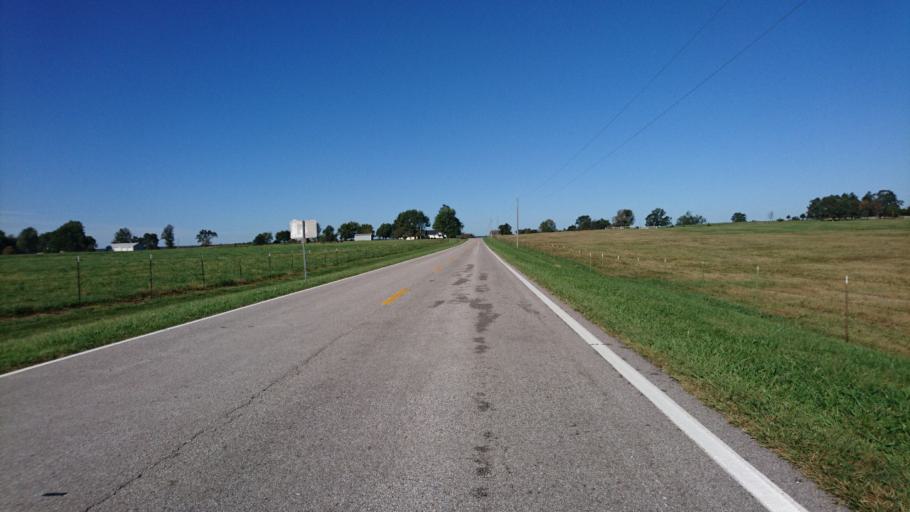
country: US
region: Missouri
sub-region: Greene County
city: Ash Grove
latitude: 37.1940
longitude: -93.6619
